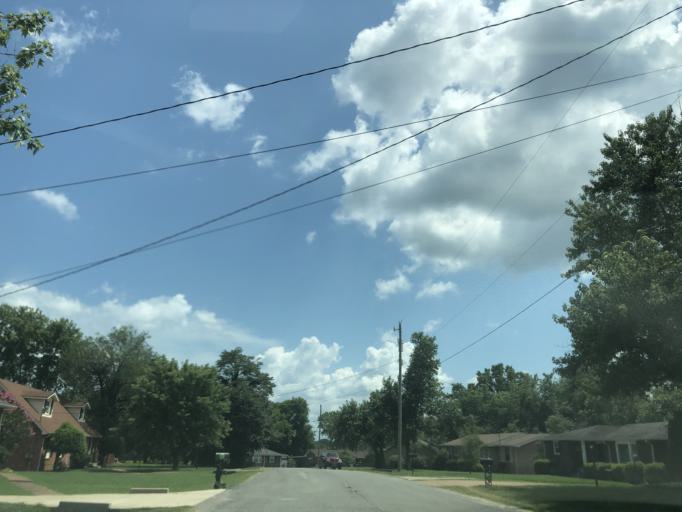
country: US
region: Tennessee
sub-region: Davidson County
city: Lakewood
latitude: 36.2028
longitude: -86.6122
